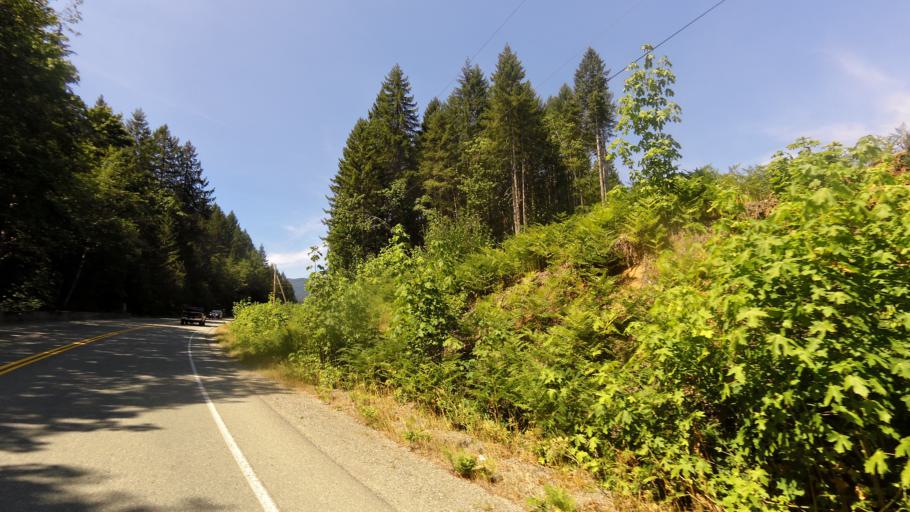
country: CA
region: British Columbia
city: Port Alberni
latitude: 49.2798
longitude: -124.9891
